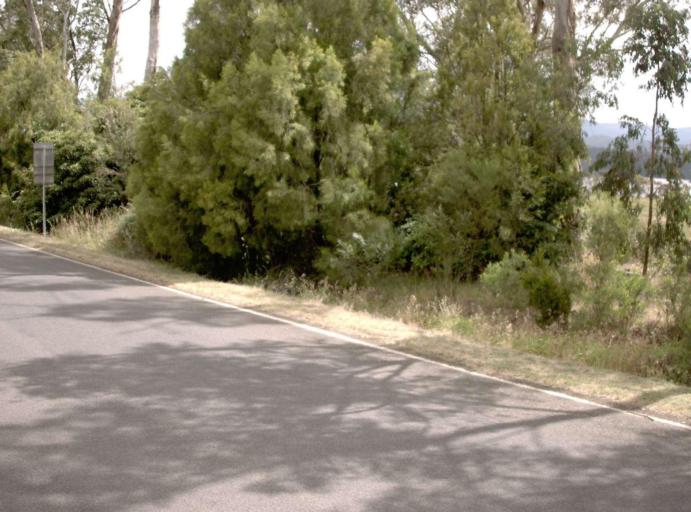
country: AU
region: Victoria
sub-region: Latrobe
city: Moe
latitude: -38.0701
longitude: 146.1765
